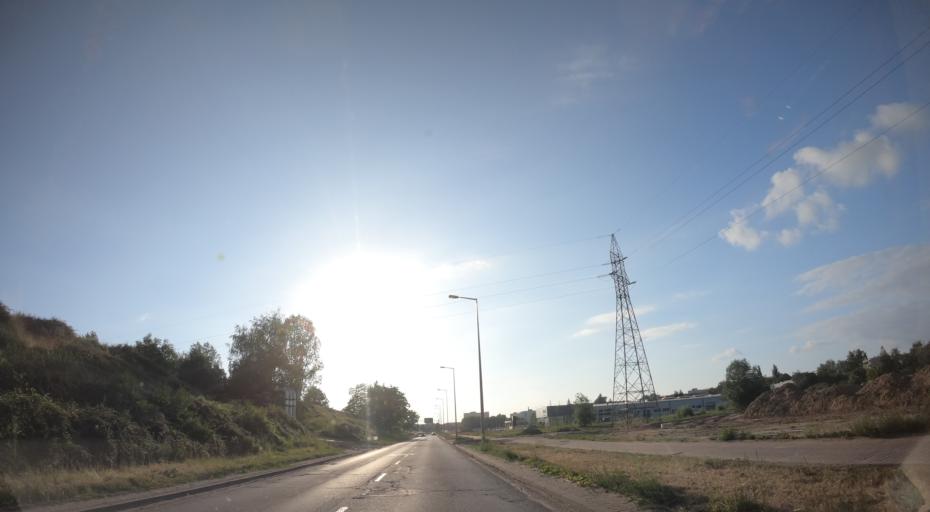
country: PL
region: Lubusz
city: Gorzow Wielkopolski
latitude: 52.7558
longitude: 15.2718
